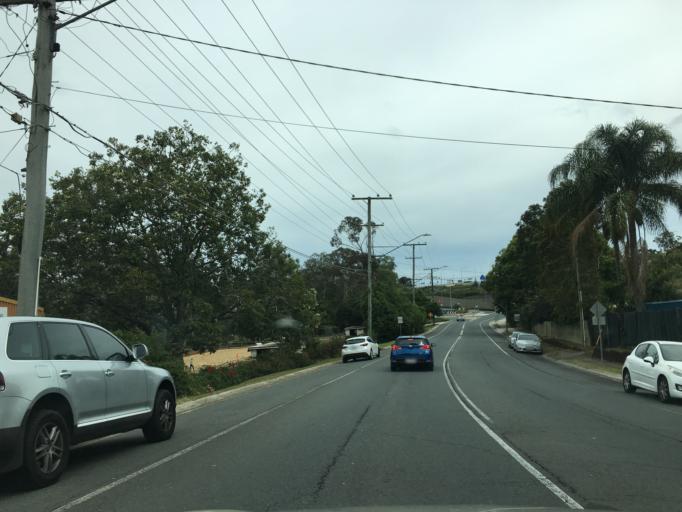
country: AU
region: Queensland
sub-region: Logan
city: Slacks Creek
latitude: -27.6472
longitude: 153.1486
